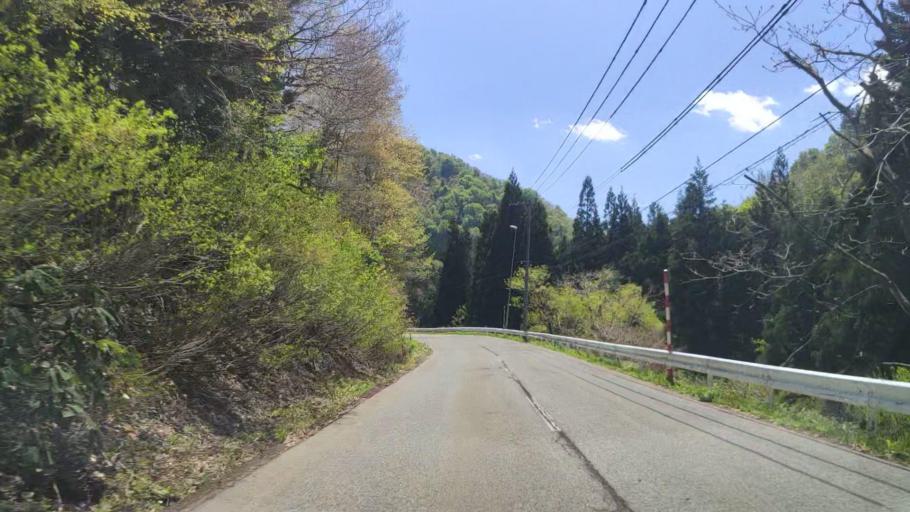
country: JP
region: Yamagata
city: Shinjo
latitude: 38.9559
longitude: 140.3580
